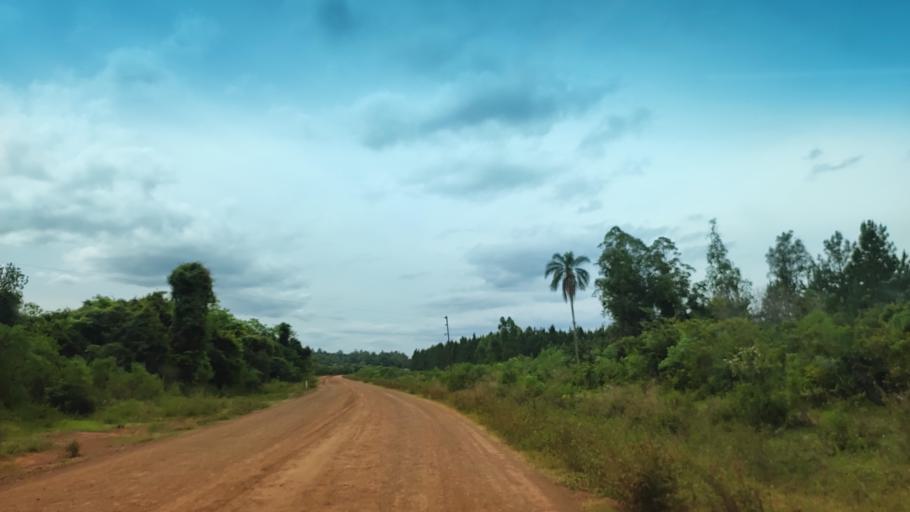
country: AR
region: Misiones
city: Garupa
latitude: -27.5050
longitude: -55.9700
